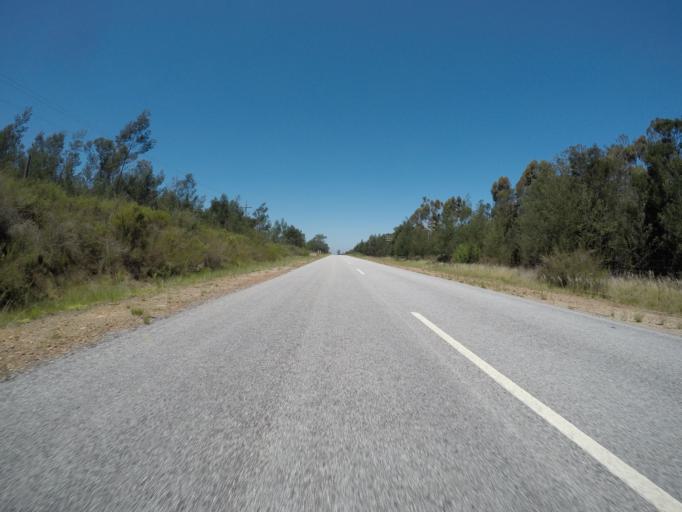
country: ZA
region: Eastern Cape
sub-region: Cacadu District Municipality
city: Kareedouw
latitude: -33.9697
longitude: 24.4594
